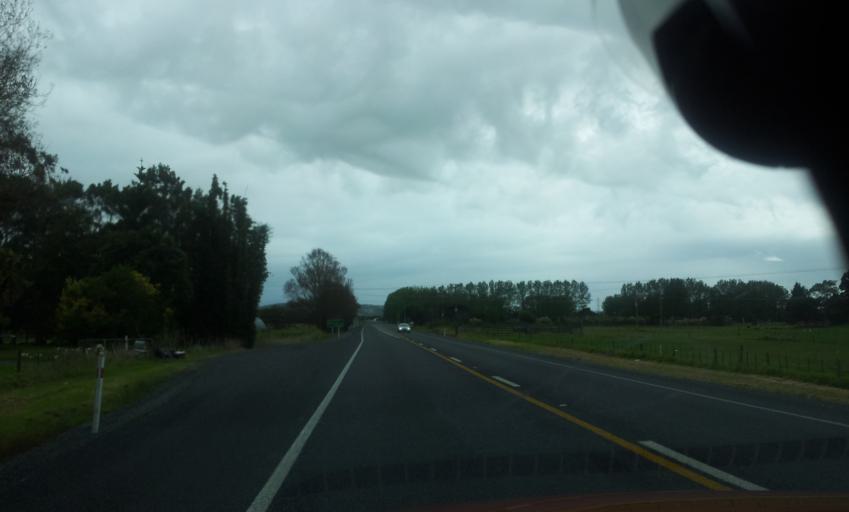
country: NZ
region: Northland
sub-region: Whangarei
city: Ruakaka
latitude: -35.9096
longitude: 174.4490
